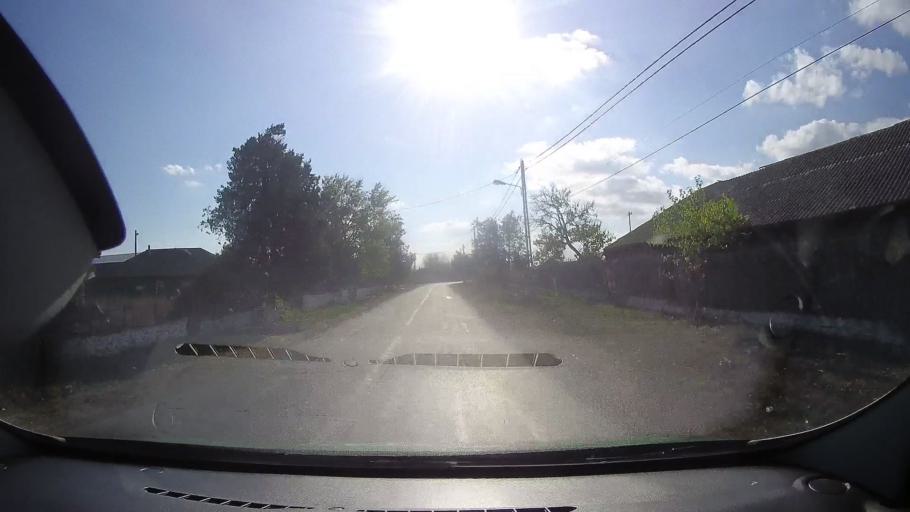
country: RO
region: Constanta
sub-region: Comuna Mihai Viteazu
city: Mihai Viteazu
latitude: 44.6274
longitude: 28.7321
